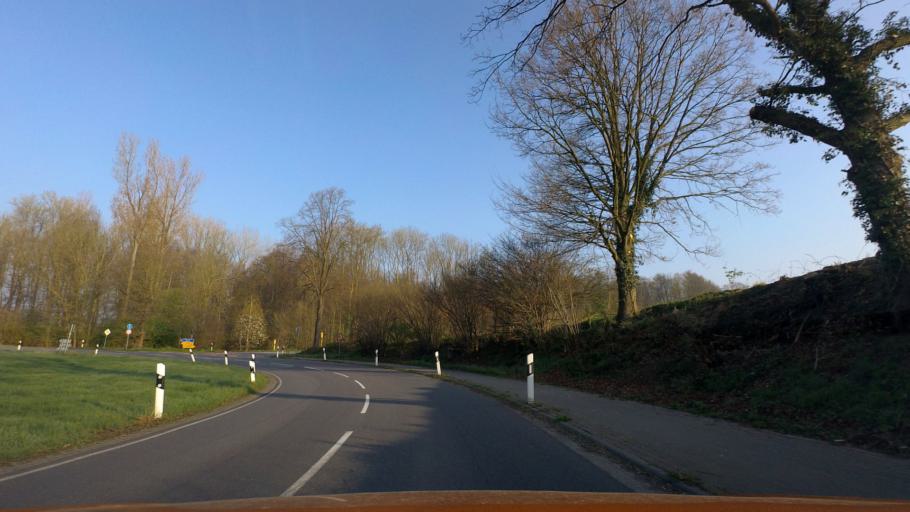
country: DE
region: Lower Saxony
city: Melle
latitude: 52.1869
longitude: 8.3809
